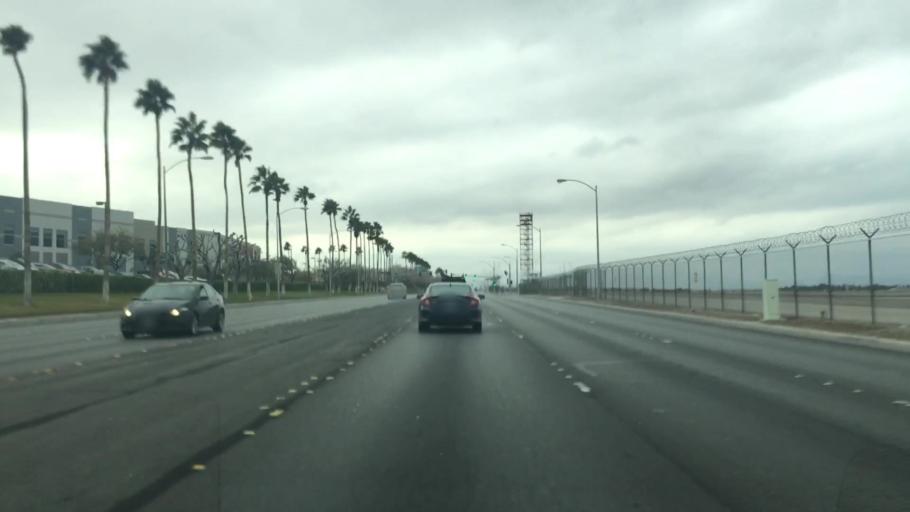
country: US
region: Nevada
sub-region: Clark County
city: Paradise
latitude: 36.0715
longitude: -115.1513
